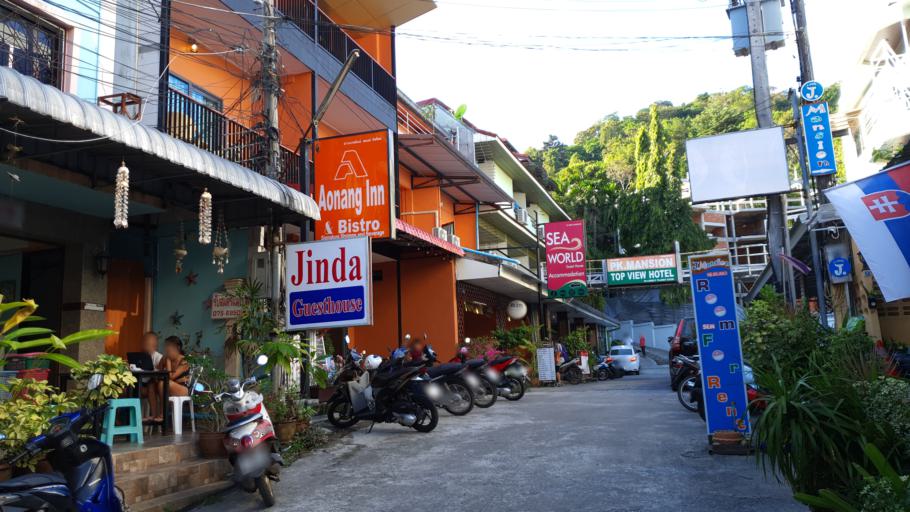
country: TH
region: Phangnga
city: Ban Ao Nang
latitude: 8.0324
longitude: 98.8230
